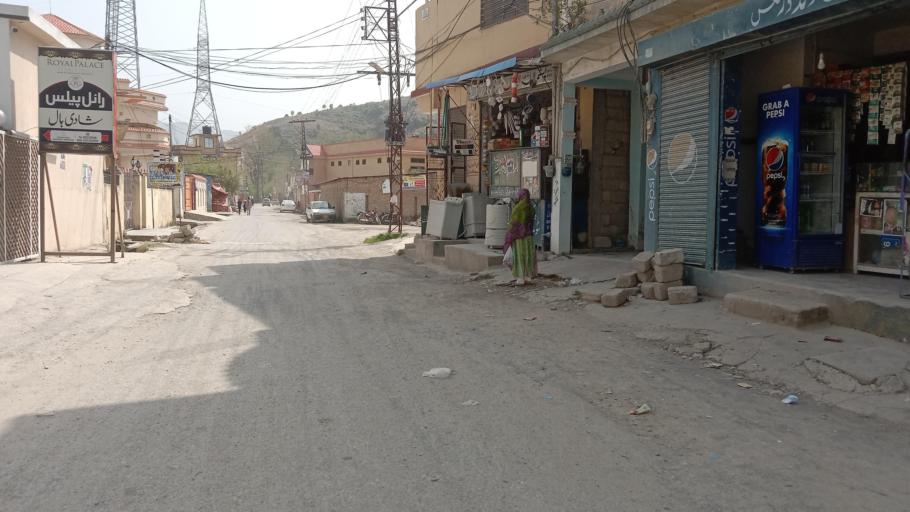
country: PK
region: Khyber Pakhtunkhwa
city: Abbottabad
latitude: 34.1564
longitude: 73.2596
